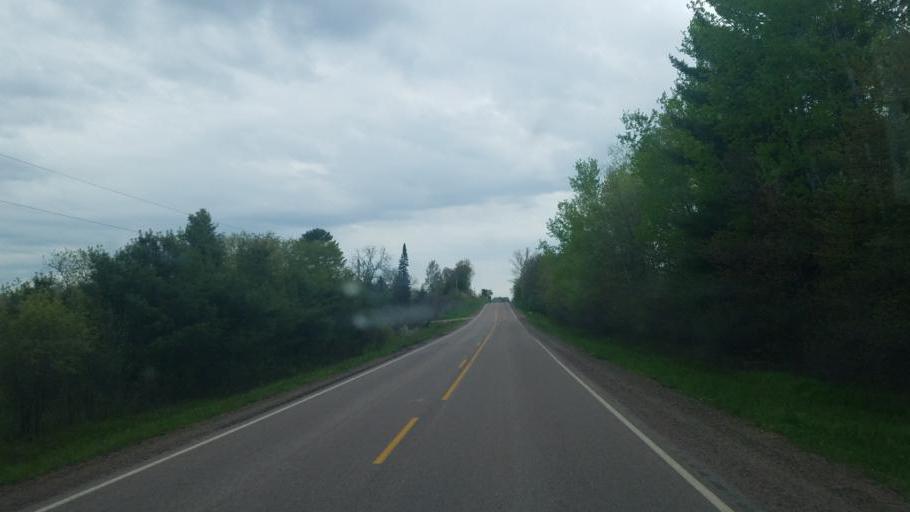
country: US
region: Wisconsin
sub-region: Wood County
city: Marshfield
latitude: 44.5718
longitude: -90.2997
